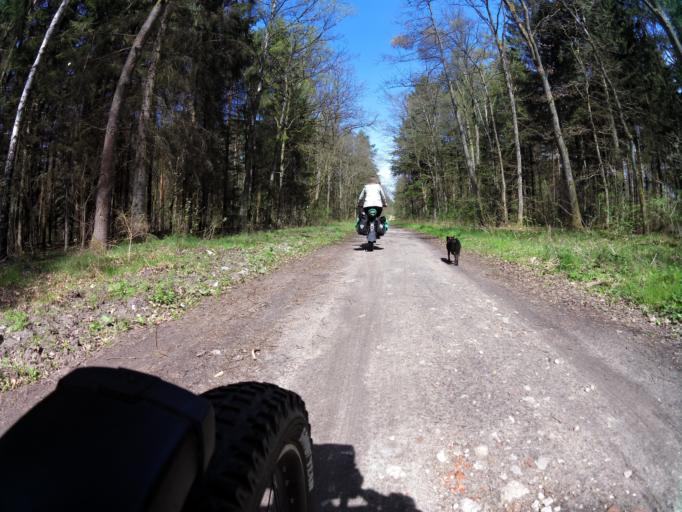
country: PL
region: West Pomeranian Voivodeship
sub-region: Powiat lobeski
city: Resko
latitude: 53.8081
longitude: 15.4472
